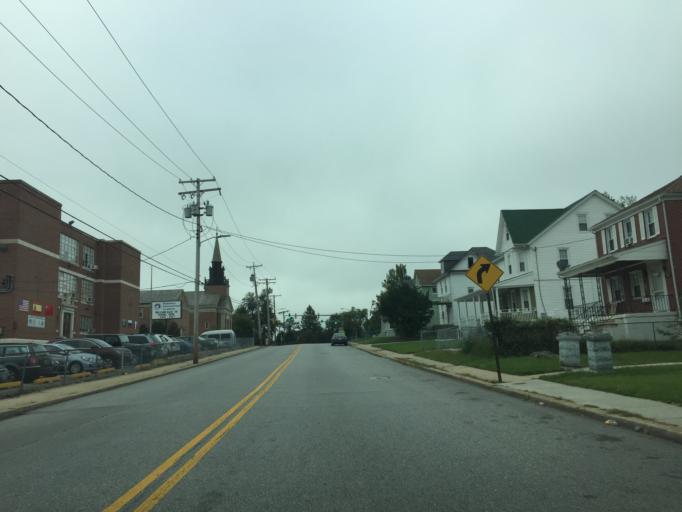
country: US
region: Maryland
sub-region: Baltimore County
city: Rosedale
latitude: 39.3362
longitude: -76.5497
